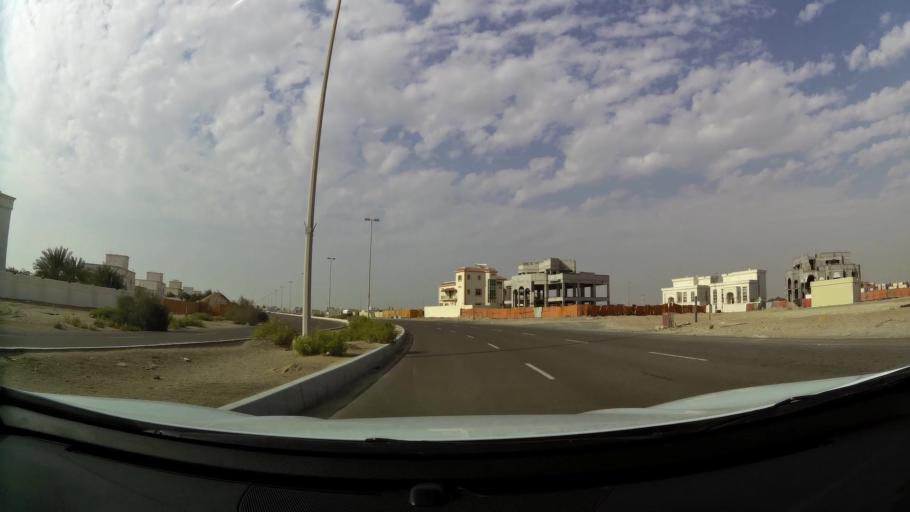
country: AE
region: Abu Dhabi
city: Abu Dhabi
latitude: 24.3333
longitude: 54.5739
